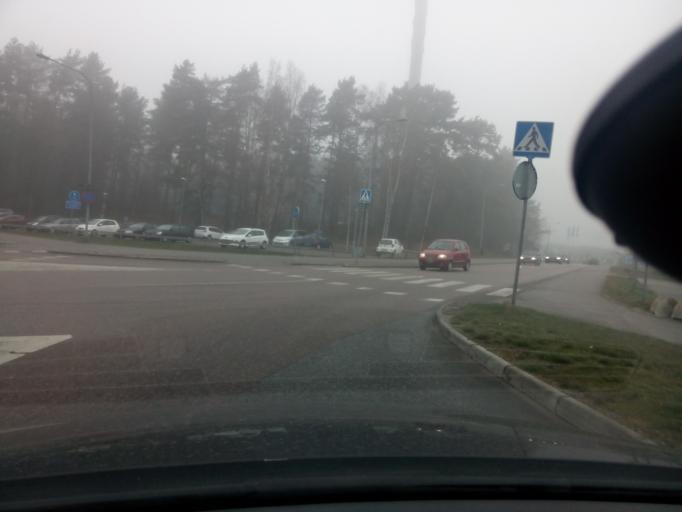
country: SE
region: Soedermanland
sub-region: Nykopings Kommun
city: Nykoping
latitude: 58.7677
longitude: 17.0247
